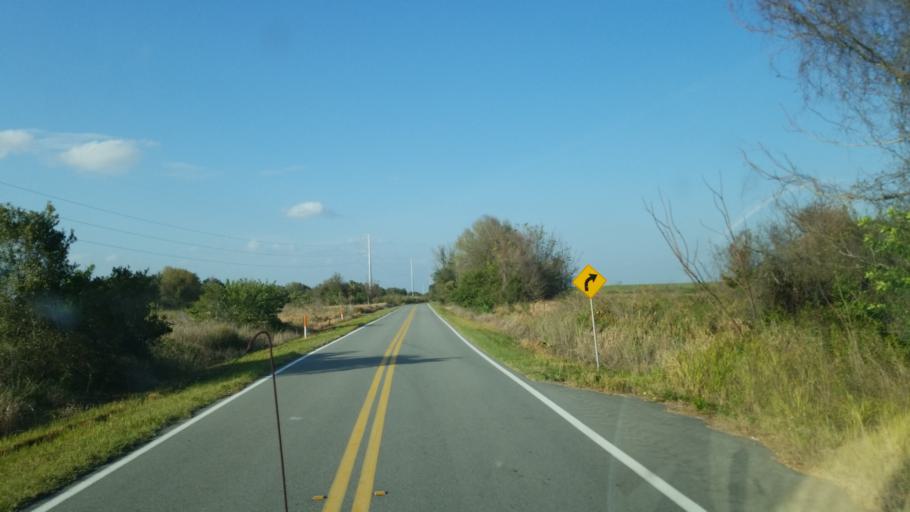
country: US
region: Florida
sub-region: Polk County
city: Mulberry
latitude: 27.7544
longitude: -81.9727
